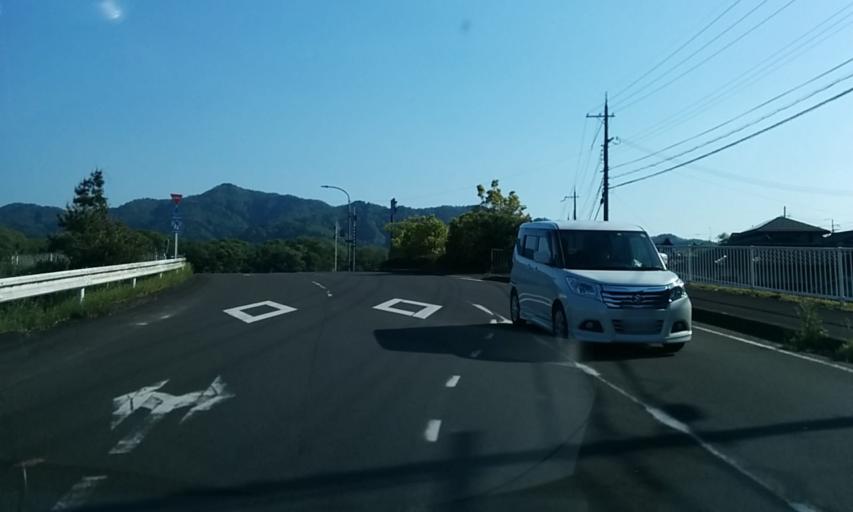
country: JP
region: Kyoto
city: Ayabe
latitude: 35.3118
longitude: 135.2079
